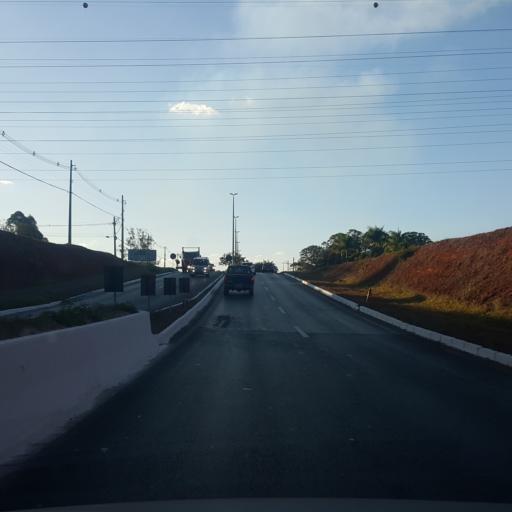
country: BR
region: Federal District
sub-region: Brasilia
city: Brasilia
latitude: -15.8373
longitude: -48.0039
